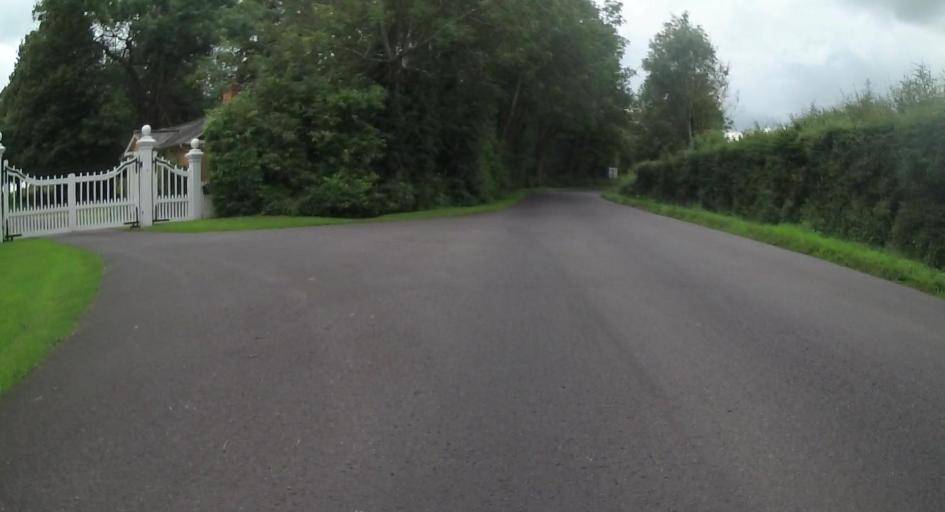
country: GB
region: England
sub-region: Wokingham
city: Swallowfield
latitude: 51.3615
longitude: -0.9903
